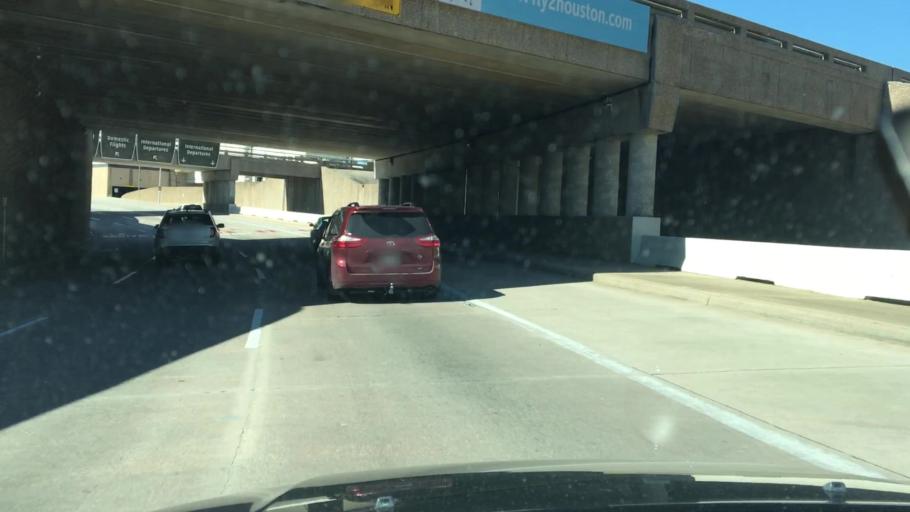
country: US
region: Texas
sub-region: Harris County
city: Humble
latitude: 29.9872
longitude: -95.3299
